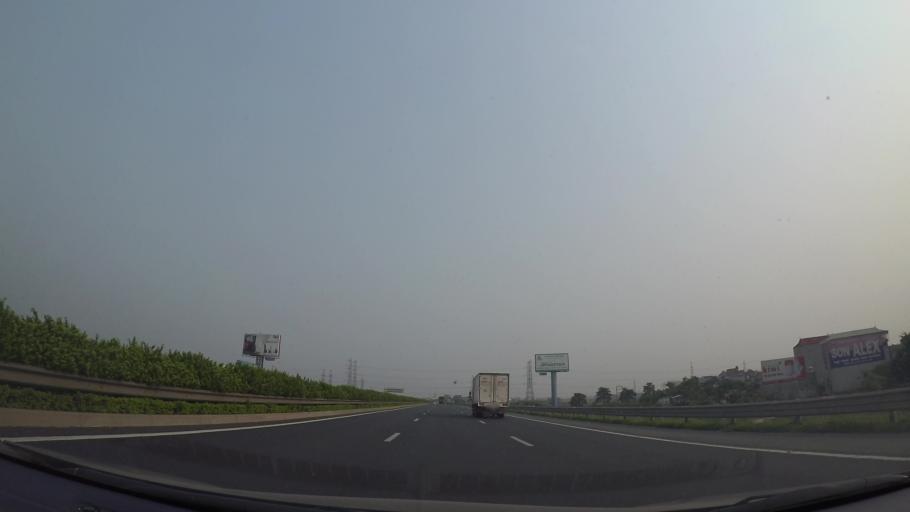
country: VN
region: Ha Noi
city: Thuong Tin
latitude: 20.8876
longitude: 105.8698
